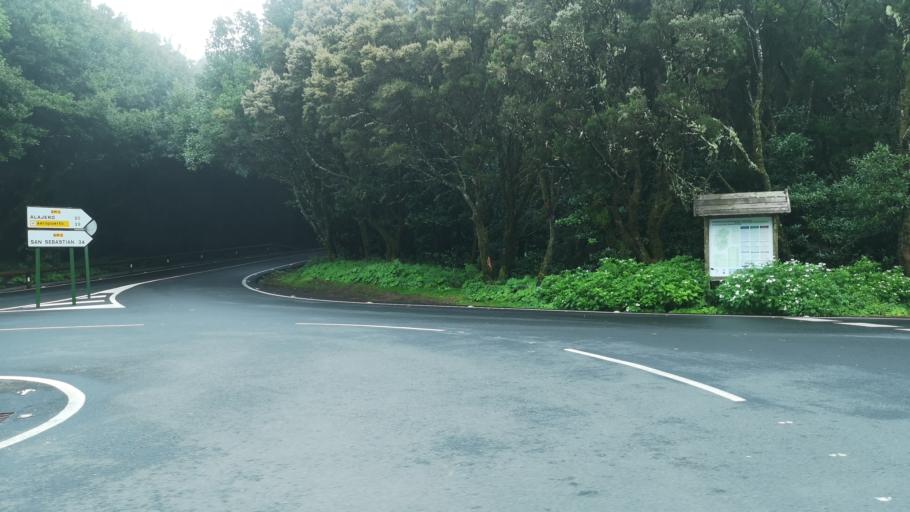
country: ES
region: Canary Islands
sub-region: Provincia de Santa Cruz de Tenerife
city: Vallehermosa
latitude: 28.1550
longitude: -17.2998
